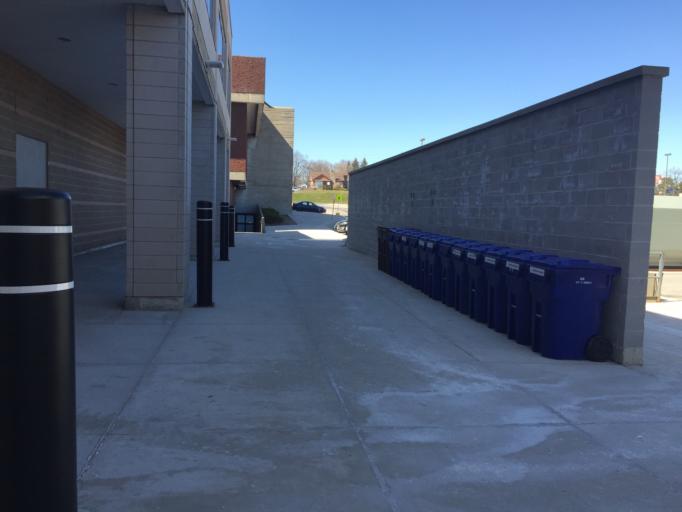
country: CA
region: Ontario
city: Oshawa
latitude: 43.8921
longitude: -78.8799
